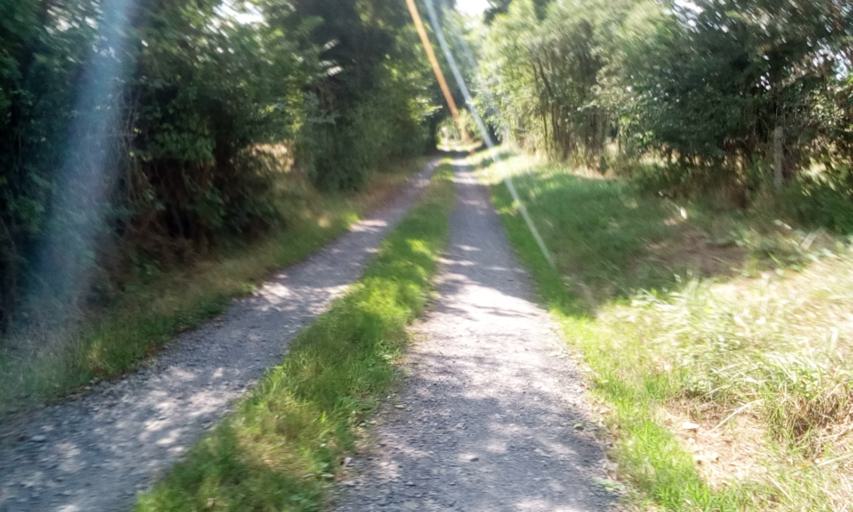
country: FR
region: Lower Normandy
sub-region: Departement du Calvados
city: Argences
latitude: 49.1317
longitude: -0.1546
